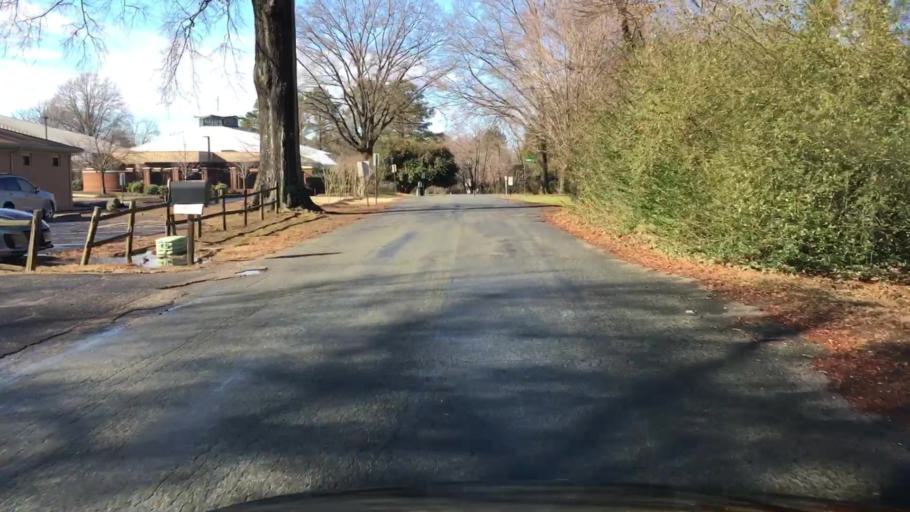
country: US
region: Virginia
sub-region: Chesterfield County
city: Bon Air
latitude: 37.5309
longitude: -77.5922
